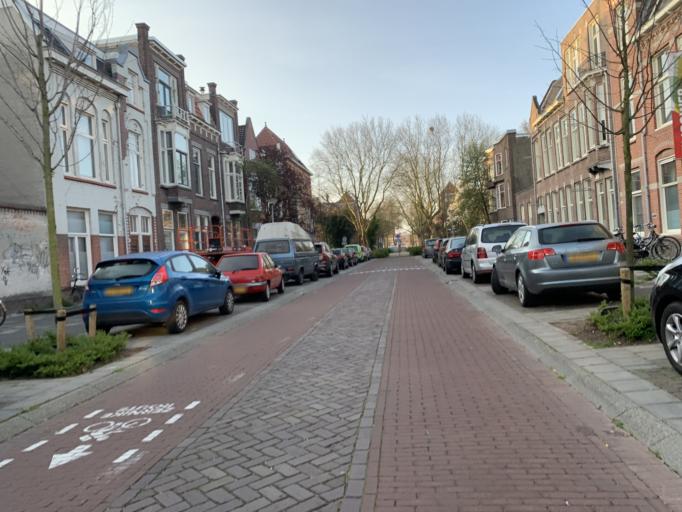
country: NL
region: Groningen
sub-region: Gemeente Groningen
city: Groningen
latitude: 53.2170
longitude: 6.5503
